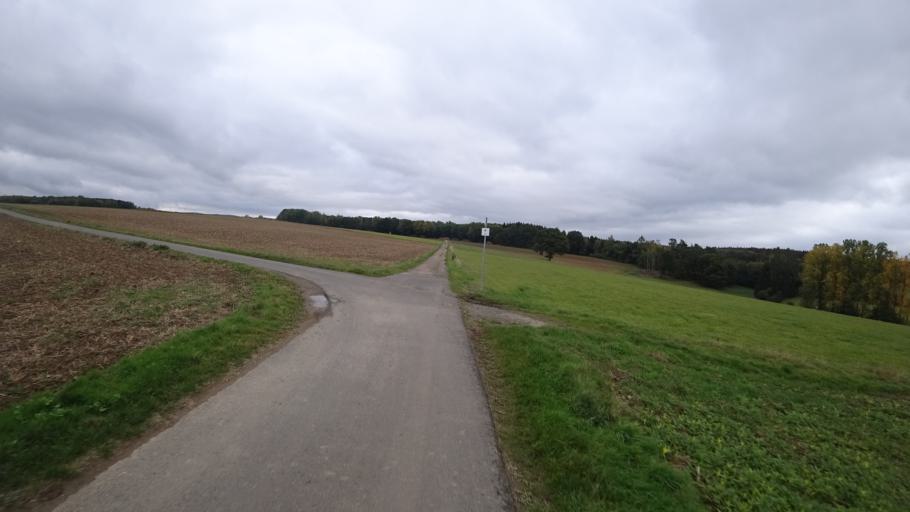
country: DE
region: Rheinland-Pfalz
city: Marienhausen
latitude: 50.5448
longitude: 7.6930
